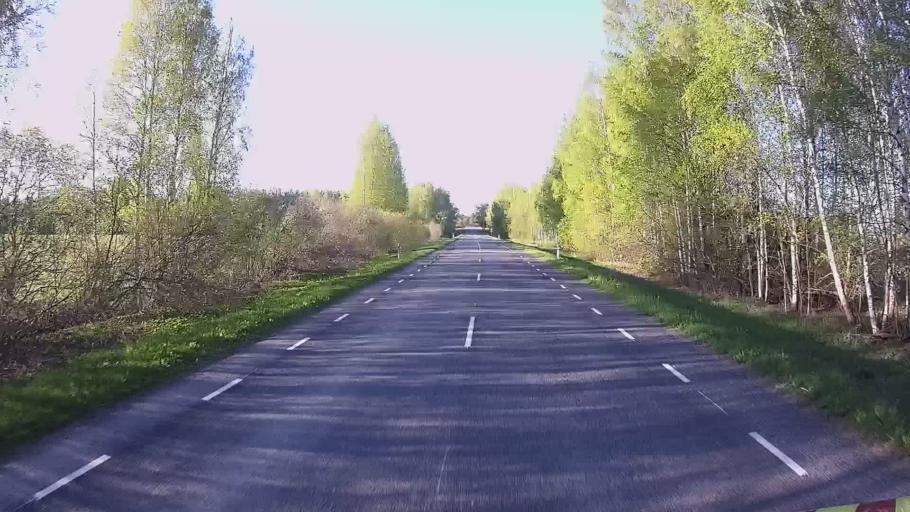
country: EE
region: Jogevamaa
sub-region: Poltsamaa linn
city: Poltsamaa
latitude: 58.5185
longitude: 25.8665
